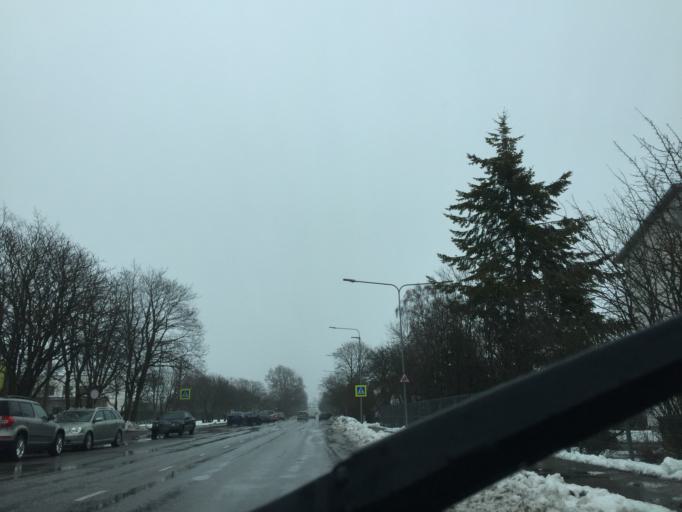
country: EE
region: Saare
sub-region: Kuressaare linn
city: Kuressaare
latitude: 58.2607
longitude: 22.4901
